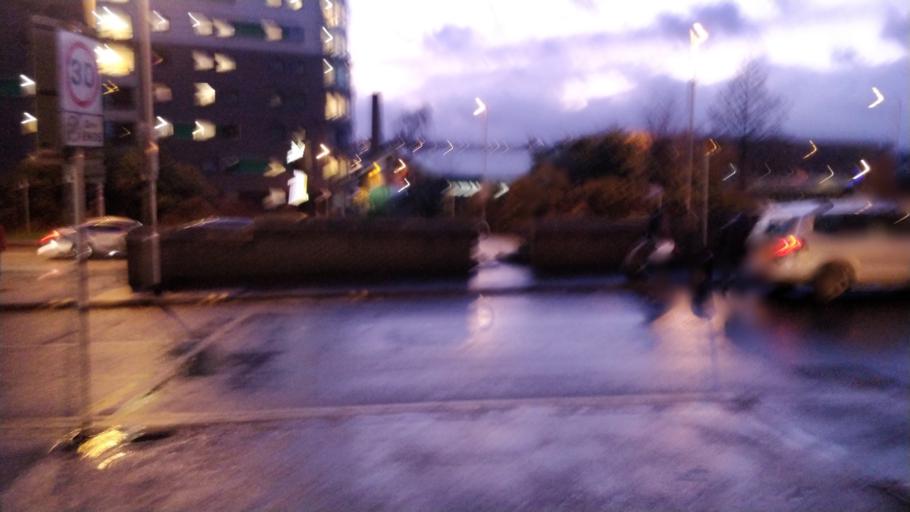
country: GB
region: England
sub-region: City and Borough of Leeds
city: Leeds
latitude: 53.8019
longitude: -1.5641
